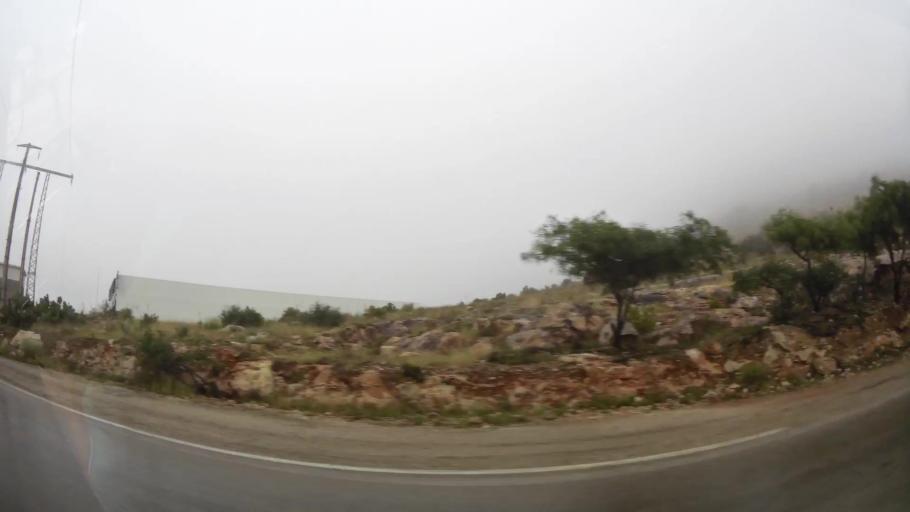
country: MA
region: Taza-Al Hoceima-Taounate
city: Al Hoceima
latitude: 35.2213
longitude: -3.9225
